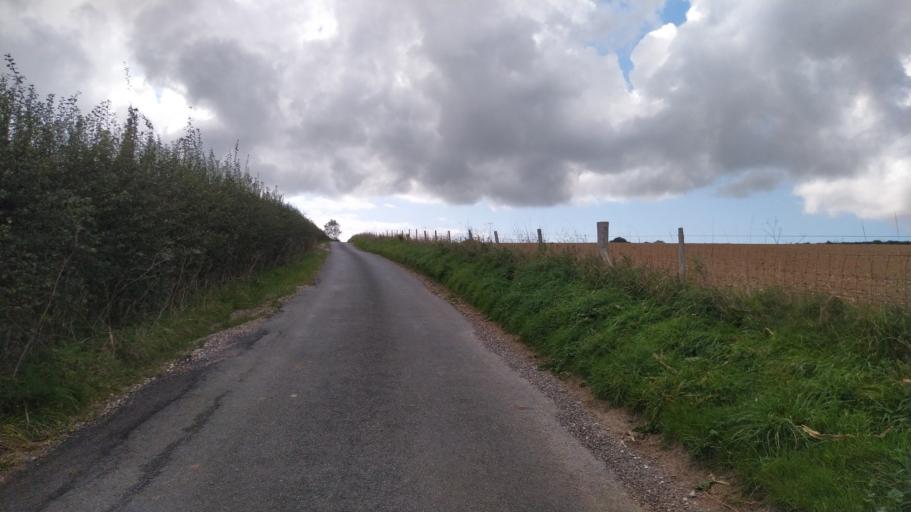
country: GB
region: England
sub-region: Dorset
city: Overcombe
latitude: 50.6757
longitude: -2.4187
